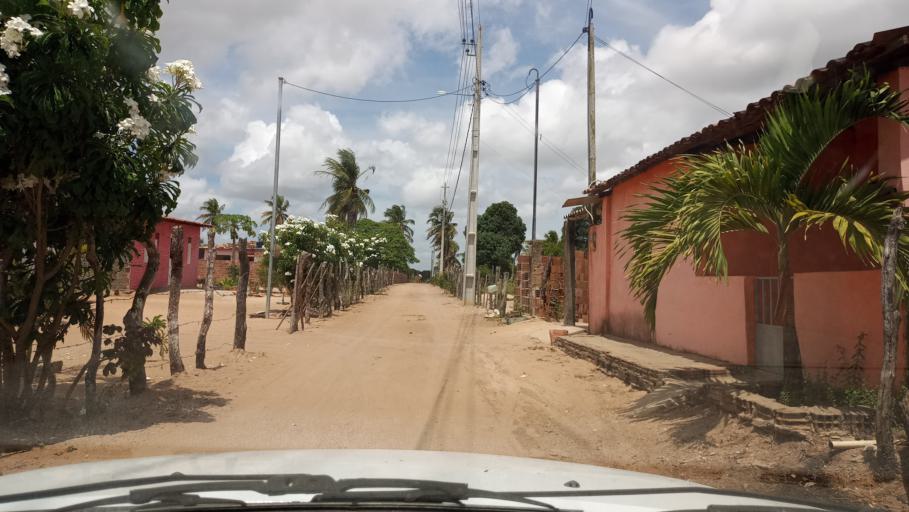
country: BR
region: Rio Grande do Norte
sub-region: Goianinha
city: Goianinha
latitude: -6.2857
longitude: -35.2836
